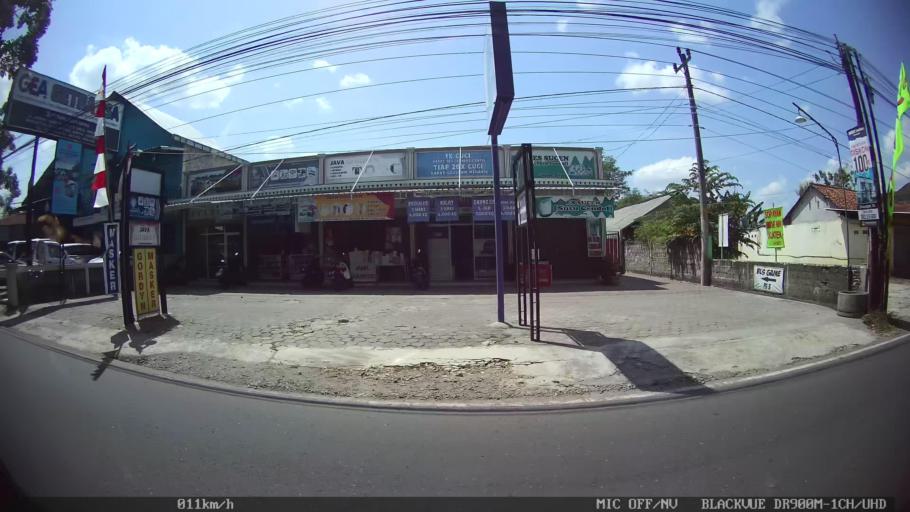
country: ID
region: Daerah Istimewa Yogyakarta
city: Sewon
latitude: -7.8479
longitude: 110.3907
